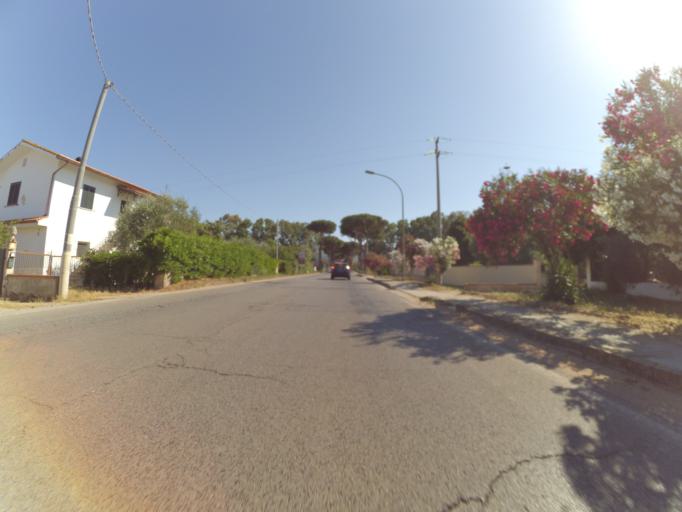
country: IT
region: Latium
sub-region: Provincia di Latina
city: San Felice Circeo
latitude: 41.2660
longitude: 13.0950
